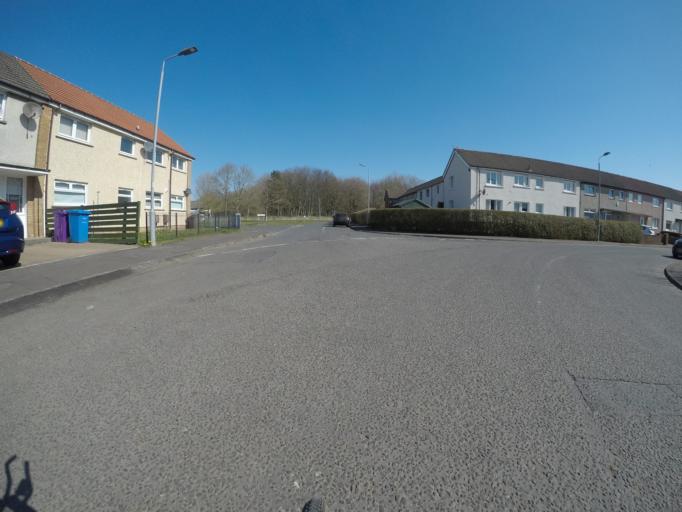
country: GB
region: Scotland
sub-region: North Ayrshire
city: Irvine
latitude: 55.6281
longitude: -4.6582
